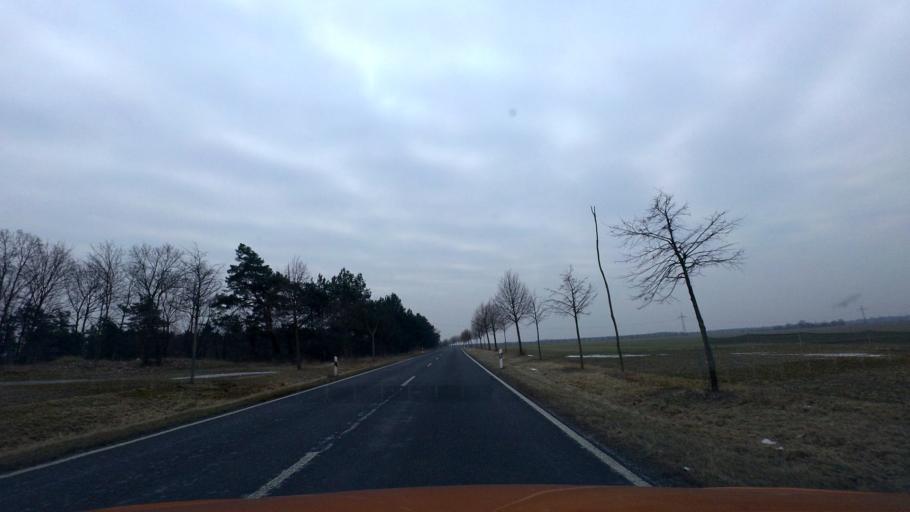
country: DE
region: Brandenburg
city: Ludwigsfelde
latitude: 52.3367
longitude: 13.2513
